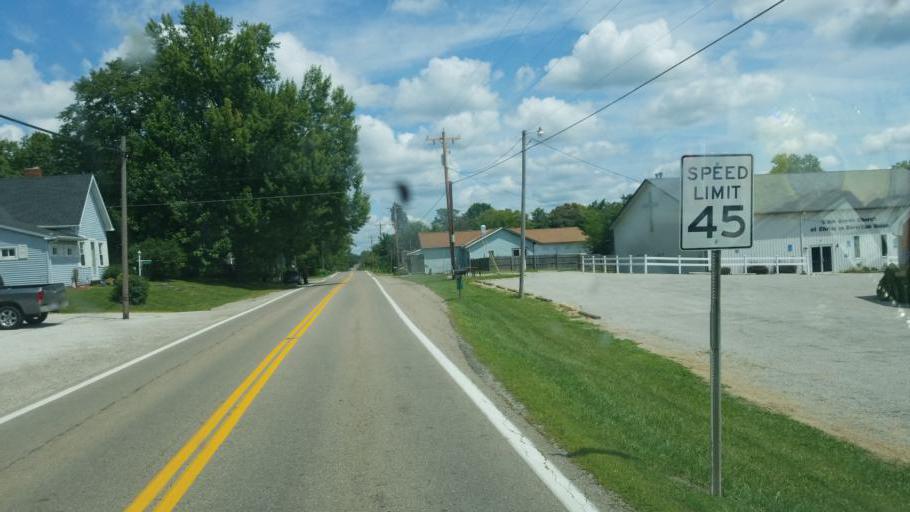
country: US
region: Ohio
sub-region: Delaware County
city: Sunbury
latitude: 40.3195
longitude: -82.8295
